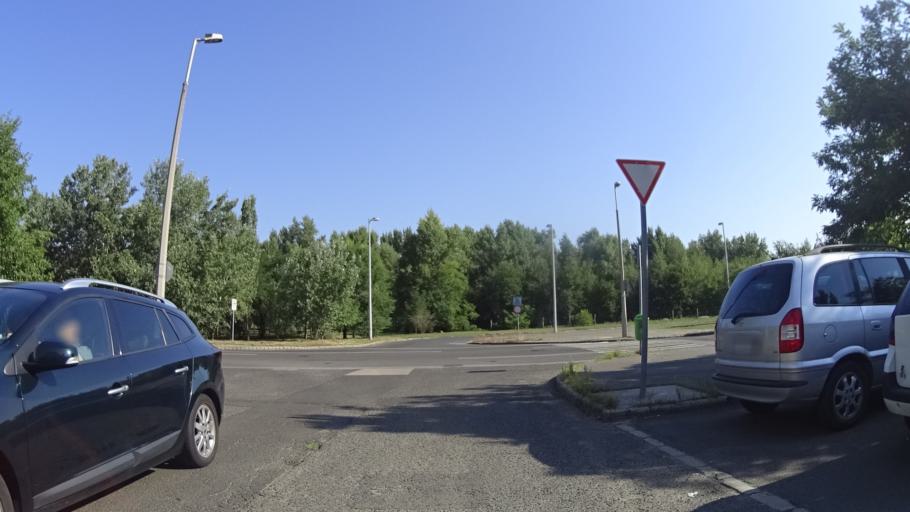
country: HU
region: Budapest
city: Budapest XV. keruelet
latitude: 47.5983
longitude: 19.1204
